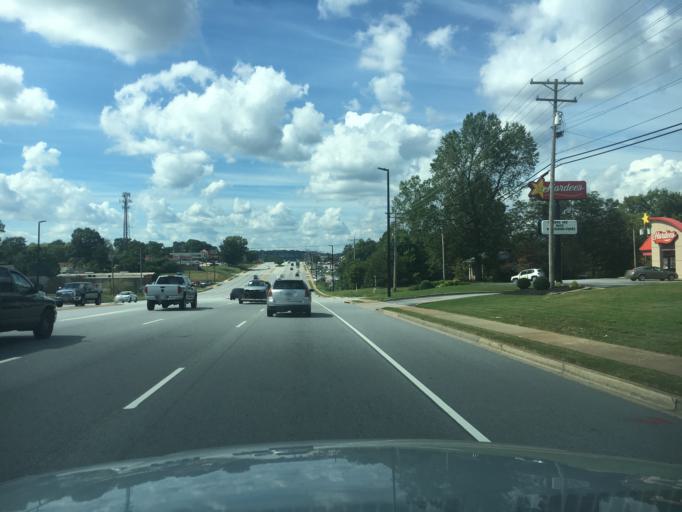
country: US
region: South Carolina
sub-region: Greenville County
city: Greer
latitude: 34.9480
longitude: -82.2181
